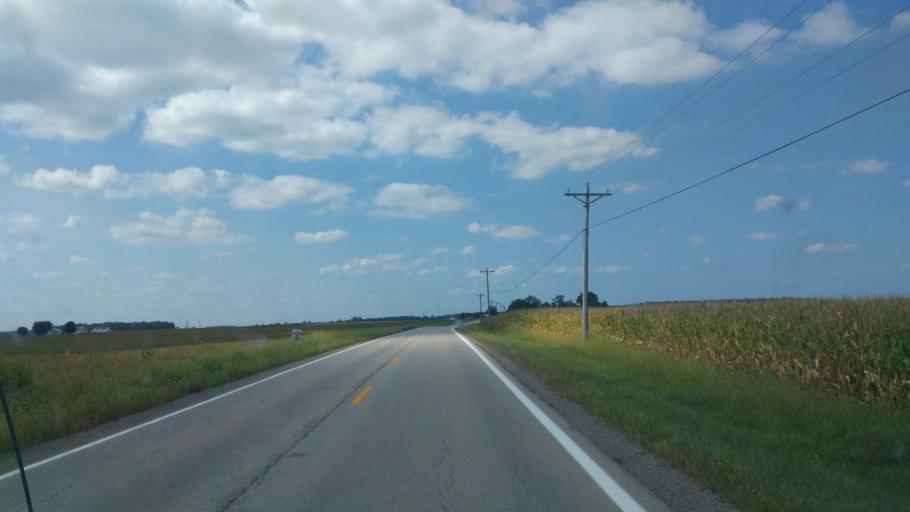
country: US
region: Ohio
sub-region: Union County
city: Richwood
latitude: 40.4197
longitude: -83.4261
